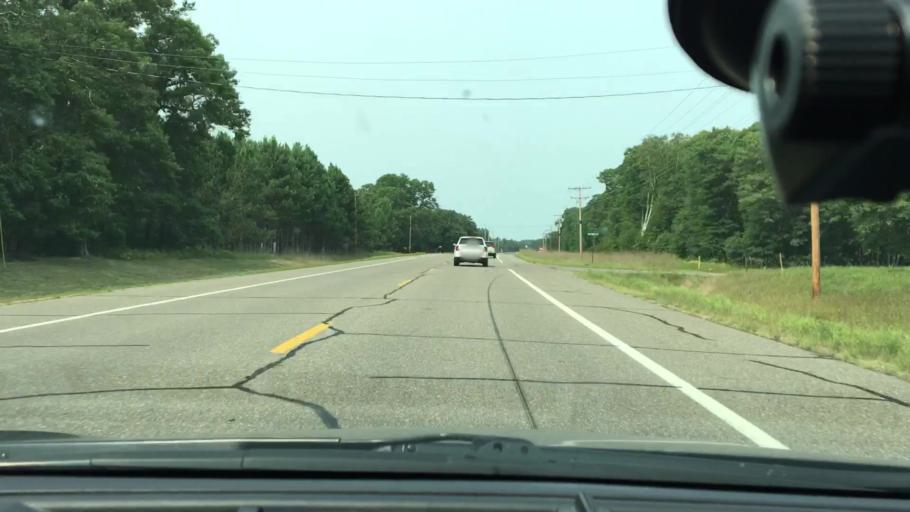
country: US
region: Minnesota
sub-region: Crow Wing County
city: Cross Lake
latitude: 46.6093
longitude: -94.1317
